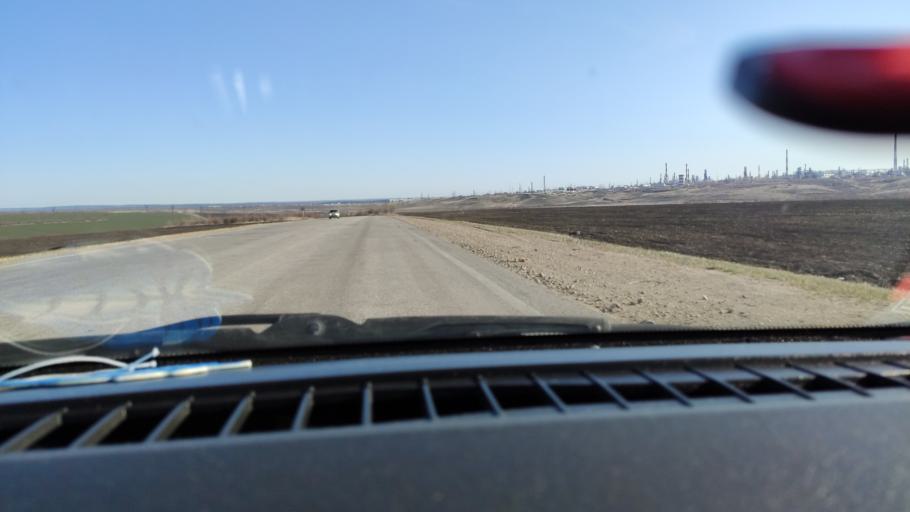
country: RU
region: Samara
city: Varlamovo
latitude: 53.0600
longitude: 48.3509
